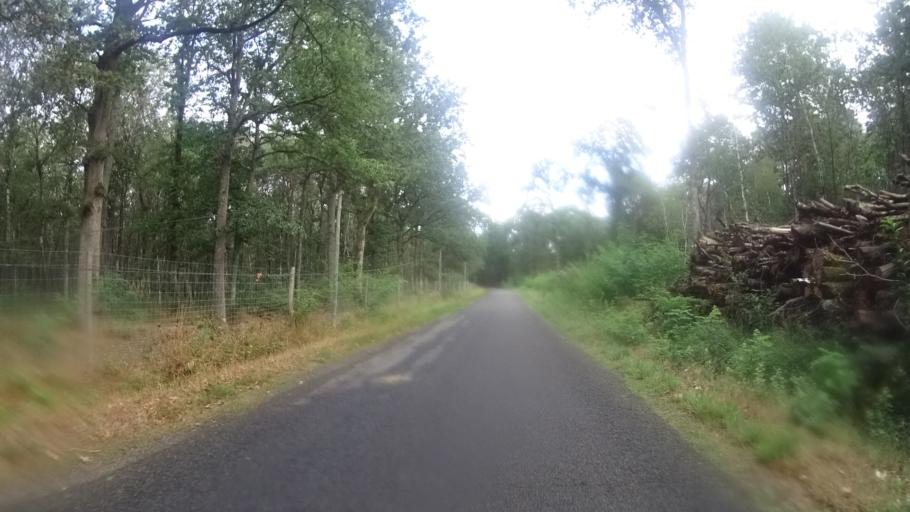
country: FR
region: Centre
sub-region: Departement du Loiret
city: Chateauneuf-sur-Loire
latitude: 47.9044
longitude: 2.2097
